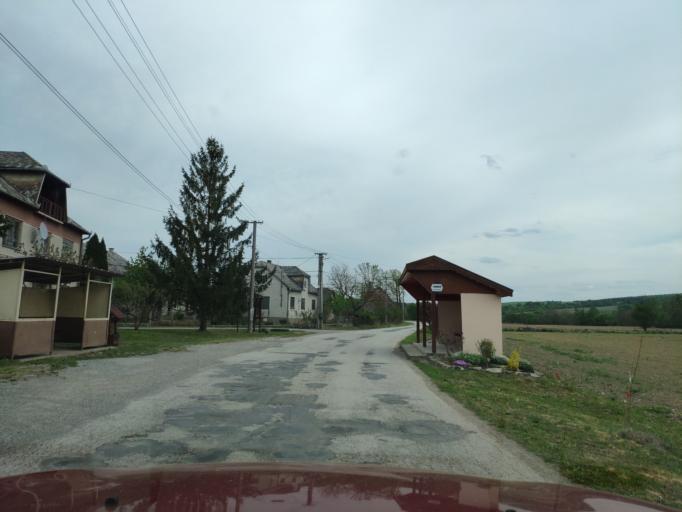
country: SK
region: Banskobystricky
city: Revuca
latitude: 48.5014
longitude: 20.2015
